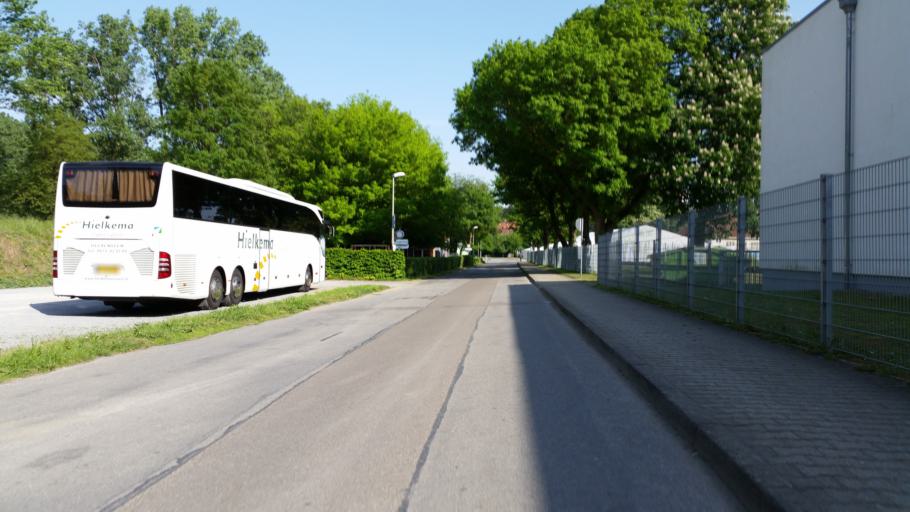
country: DE
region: Baden-Wuerttemberg
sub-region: Regierungsbezirk Stuttgart
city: Freiberg am Neckar
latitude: 48.9401
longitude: 9.1997
